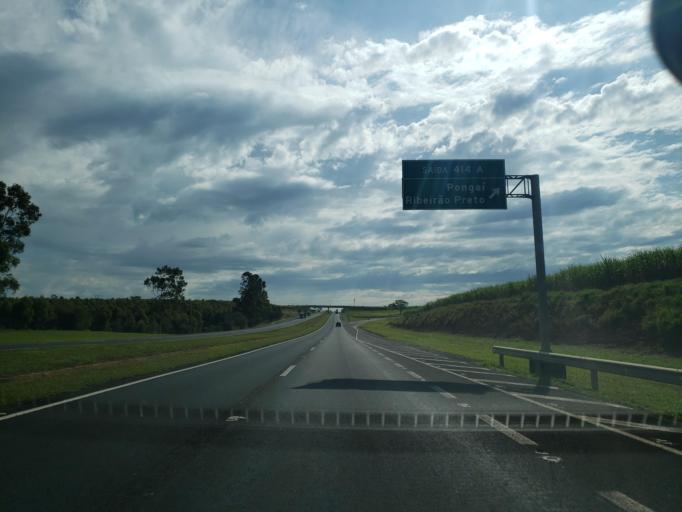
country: BR
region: Sao Paulo
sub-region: Cafelandia
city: Cafelandia
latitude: -21.8789
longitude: -49.5560
